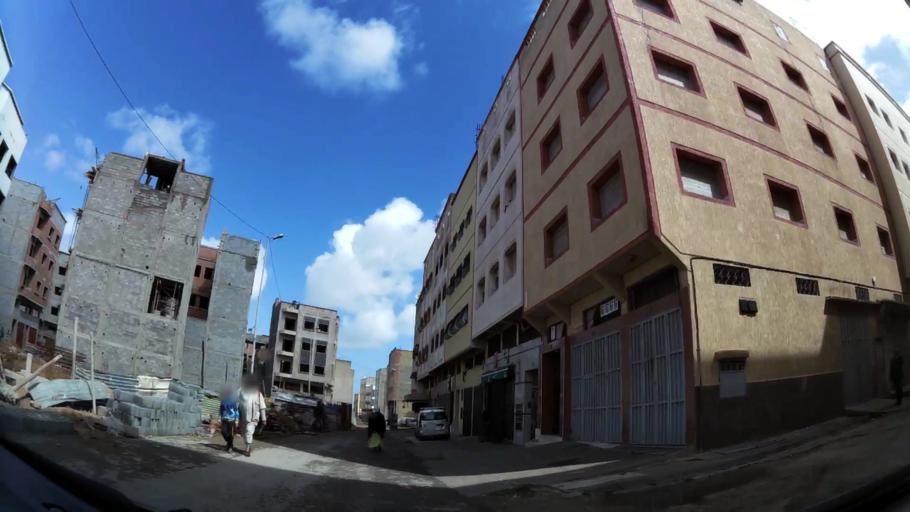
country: MA
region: Grand Casablanca
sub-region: Casablanca
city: Casablanca
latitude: 33.5367
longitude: -7.5787
